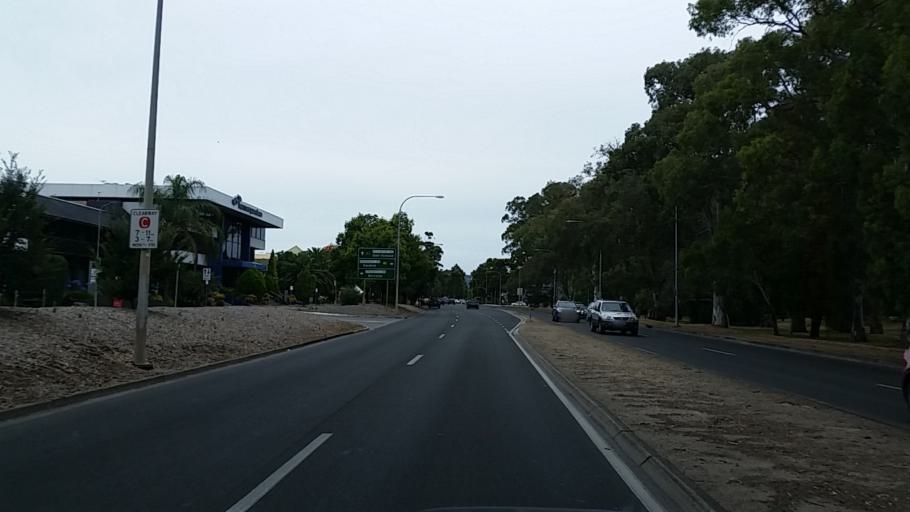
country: AU
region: South Australia
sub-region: Unley
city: Fullarton
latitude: -34.9378
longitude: 138.6242
